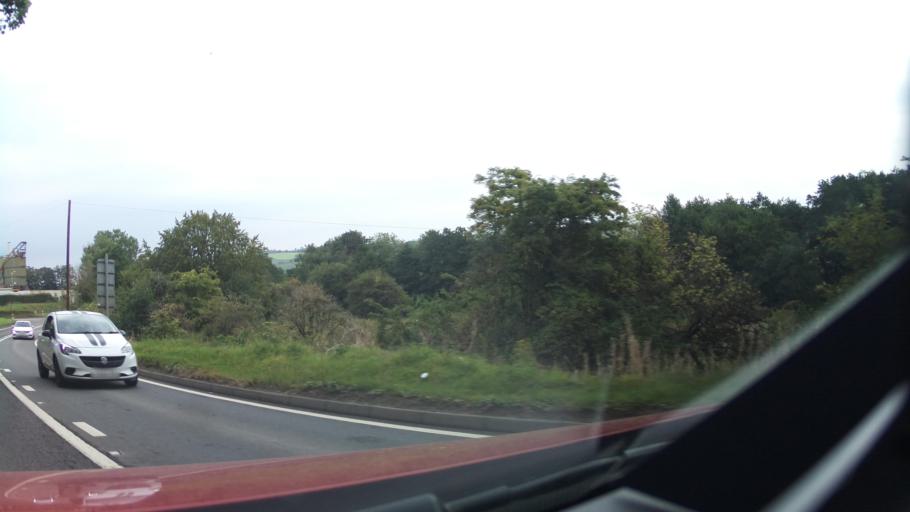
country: GB
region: Scotland
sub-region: Dumfries and Galloway
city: Locharbriggs
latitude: 55.1122
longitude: -3.5788
